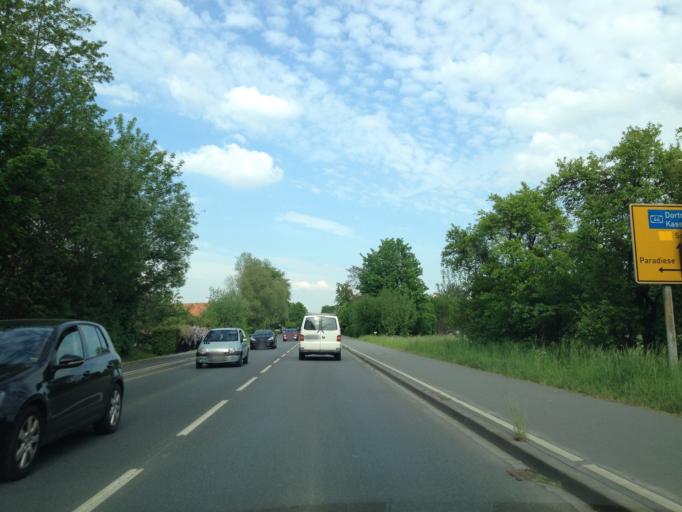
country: DE
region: North Rhine-Westphalia
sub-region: Regierungsbezirk Arnsberg
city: Soest
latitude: 51.5557
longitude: 8.0618
